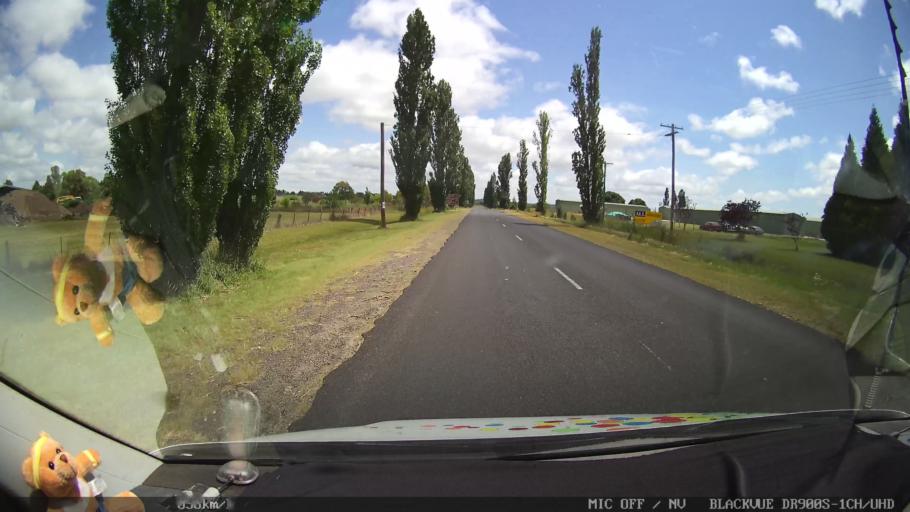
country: AU
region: New South Wales
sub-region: Glen Innes Severn
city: Glen Innes
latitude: -29.7242
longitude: 151.7261
